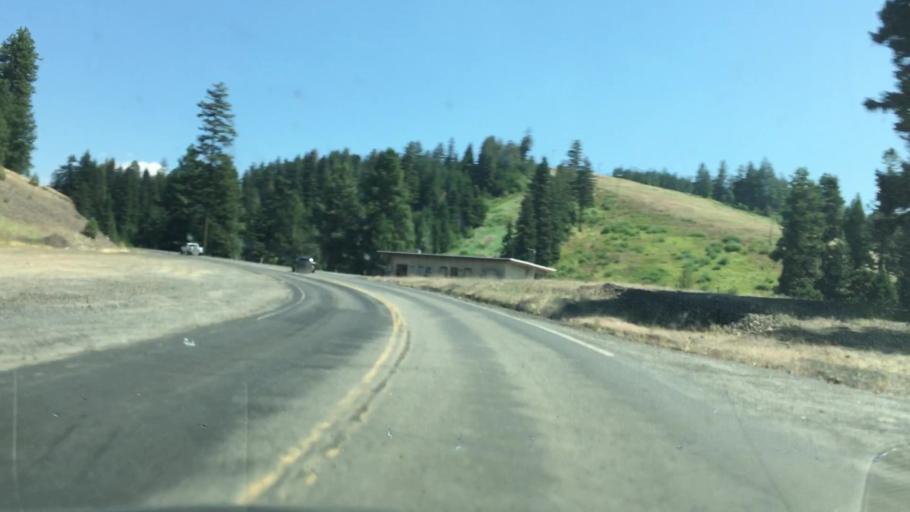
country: US
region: Idaho
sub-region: Valley County
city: McCall
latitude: 44.9308
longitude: -116.1637
